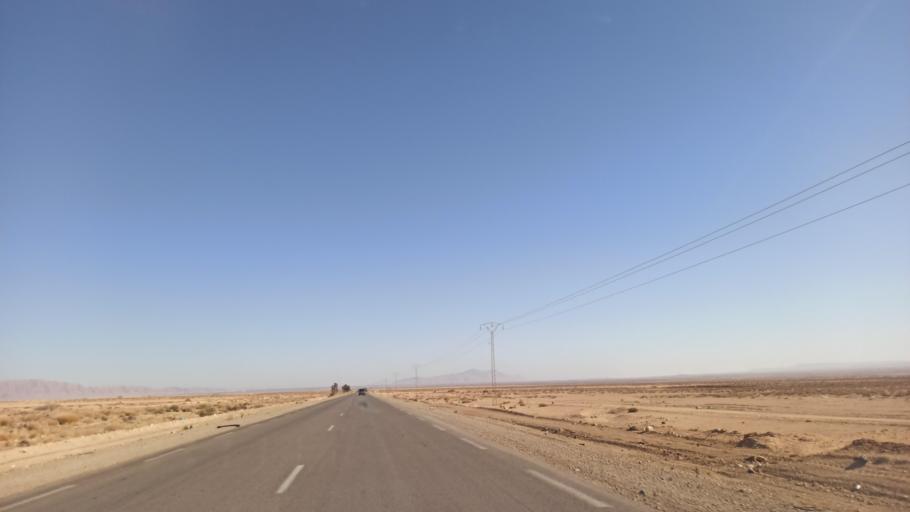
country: TN
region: Gafsa
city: Al Metlaoui
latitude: 34.3201
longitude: 8.5173
